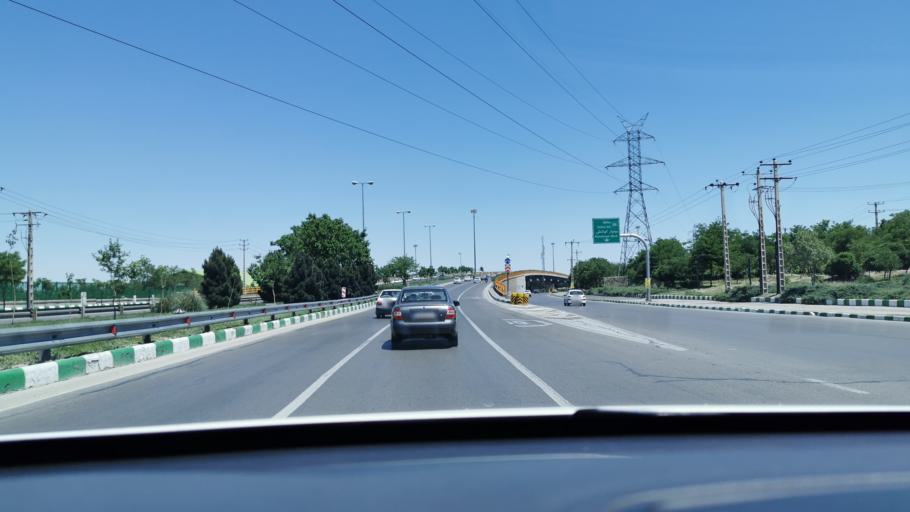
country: IR
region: Razavi Khorasan
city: Mashhad
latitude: 36.2568
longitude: 59.5946
